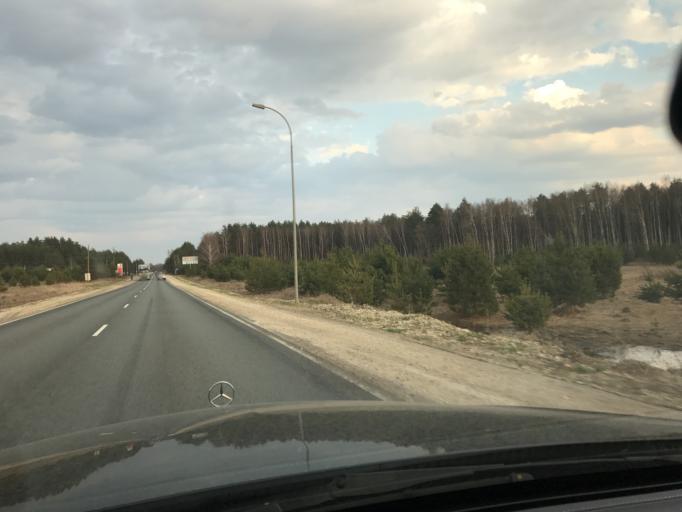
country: RU
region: Vladimir
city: Murom
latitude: 55.6224
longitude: 41.9052
